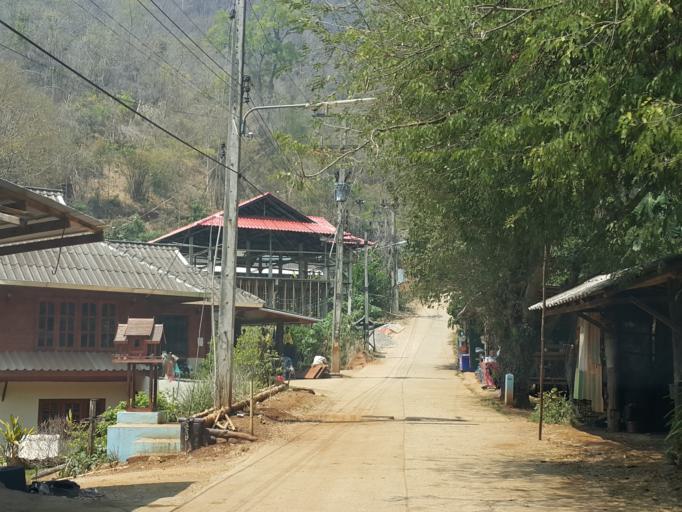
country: TH
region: Chiang Mai
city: Samoeng
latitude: 18.7992
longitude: 98.7936
